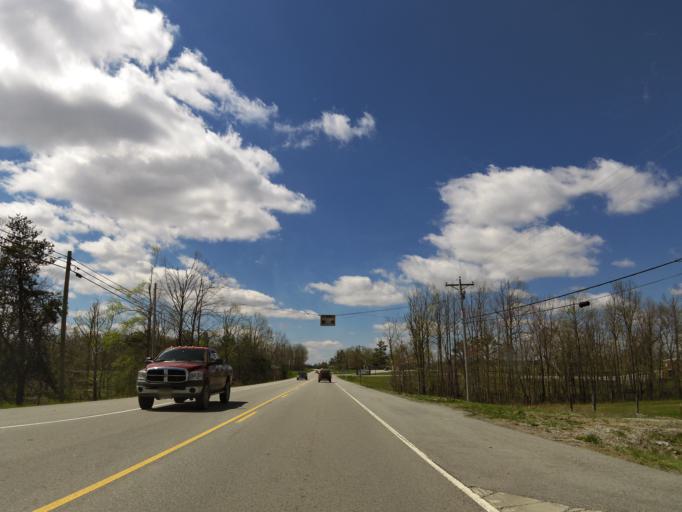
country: US
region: Tennessee
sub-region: White County
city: Sparta
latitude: 35.9419
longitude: -85.3288
